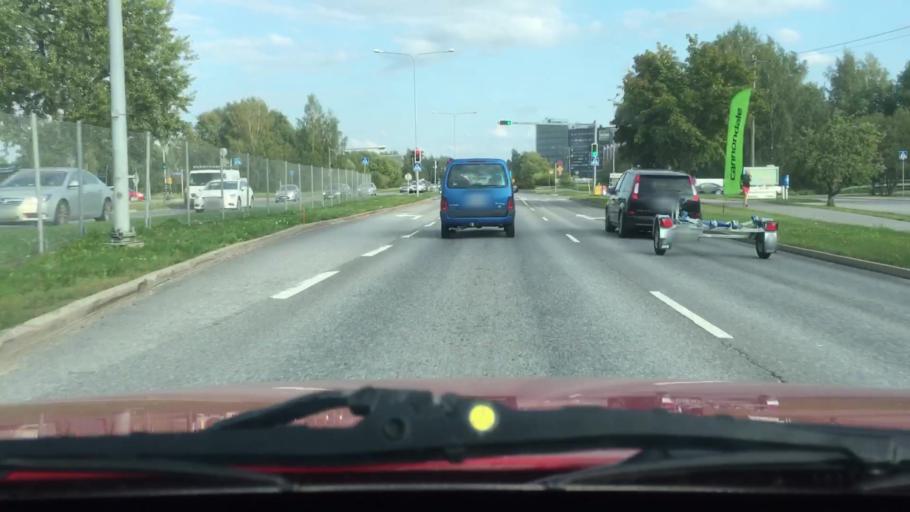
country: FI
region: Varsinais-Suomi
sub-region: Turku
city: Turku
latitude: 60.4575
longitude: 22.2269
